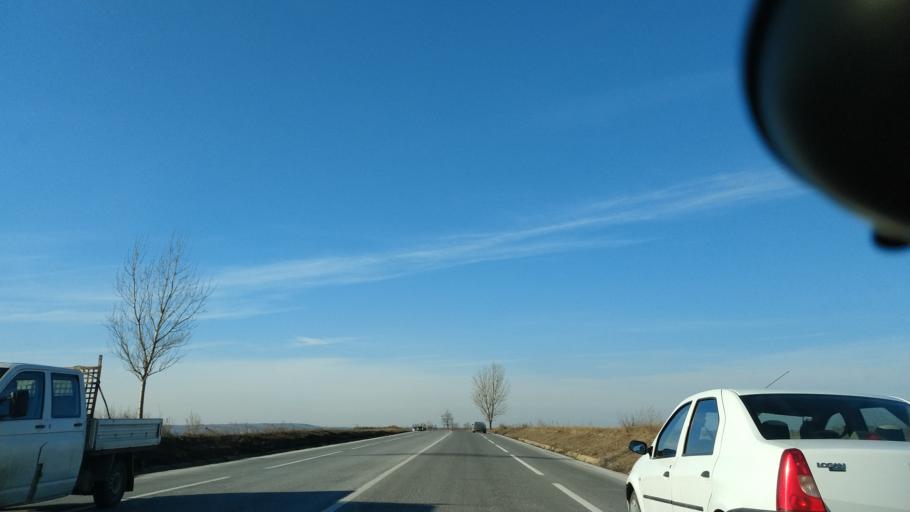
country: RO
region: Iasi
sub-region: Comuna Podu Iloaiei
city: Budai
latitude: 47.2232
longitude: 27.1948
